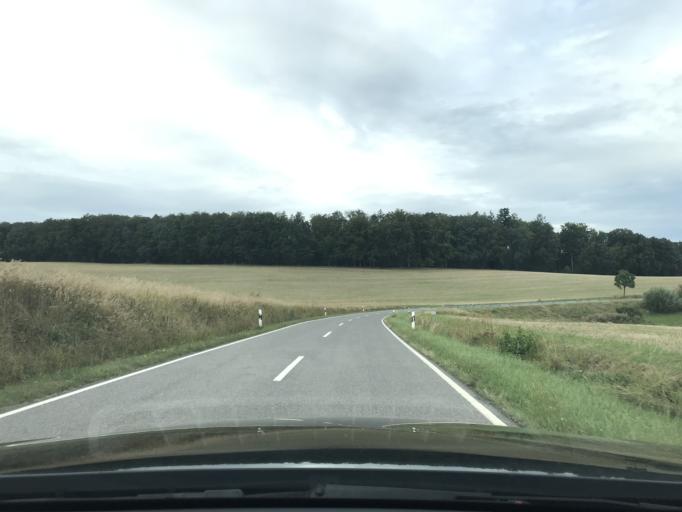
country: DE
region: Bavaria
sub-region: Regierungsbezirk Unterfranken
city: Zeil
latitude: 50.0357
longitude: 10.6347
